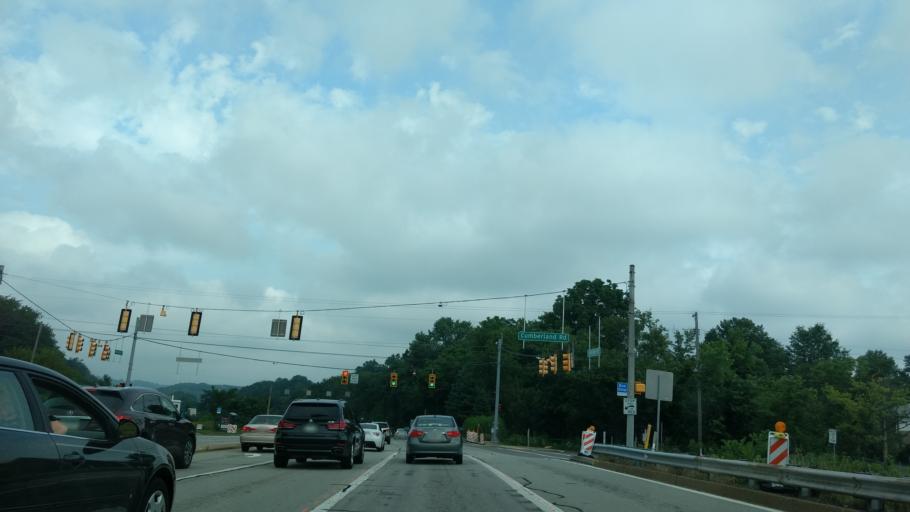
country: US
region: Pennsylvania
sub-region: Allegheny County
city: West View
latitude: 40.5717
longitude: -80.0234
